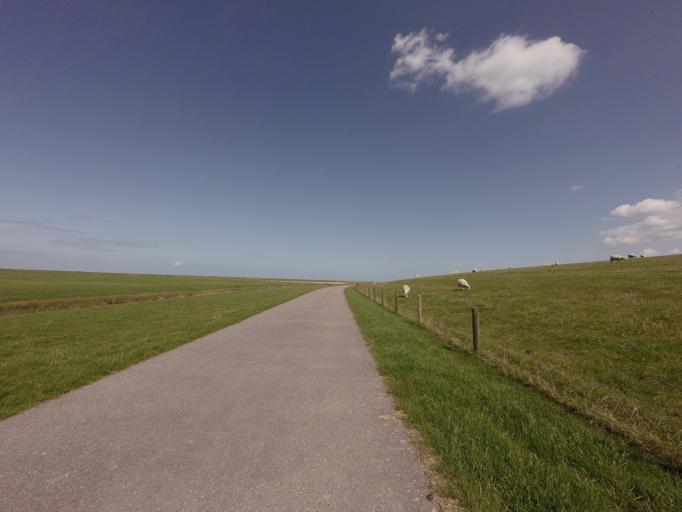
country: NL
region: Friesland
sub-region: Gemeente Ferwerderadiel
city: Marrum
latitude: 53.3363
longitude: 5.7823
